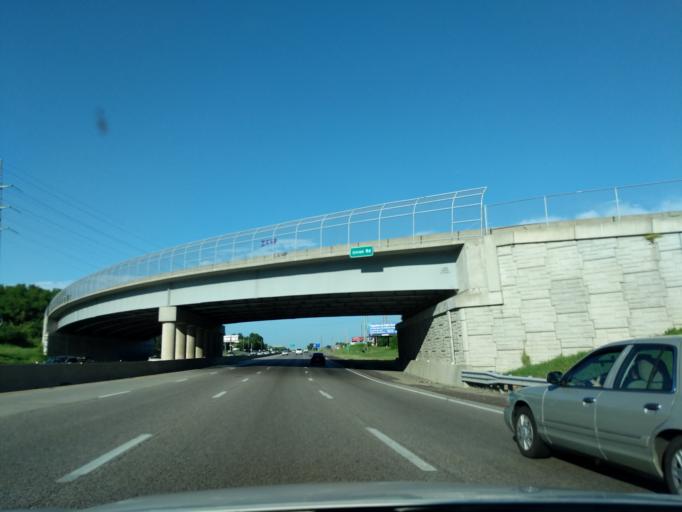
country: US
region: Missouri
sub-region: Saint Louis County
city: Saint George
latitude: 38.5405
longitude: -90.3035
